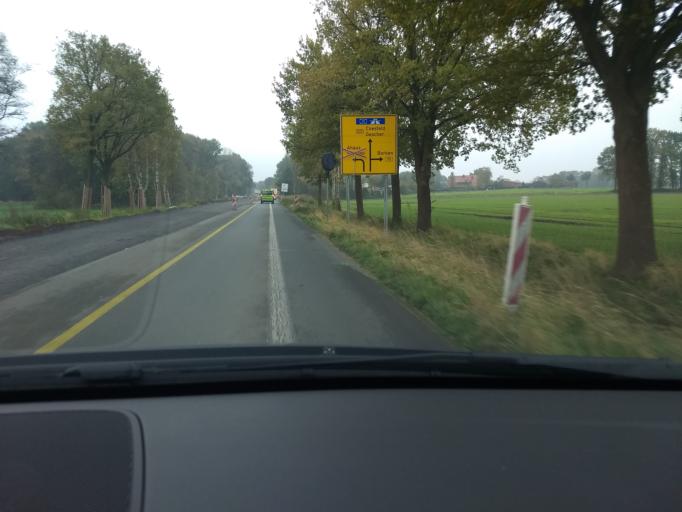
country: DE
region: North Rhine-Westphalia
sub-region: Regierungsbezirk Munster
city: Sudlohn
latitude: 51.9291
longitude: 6.8413
